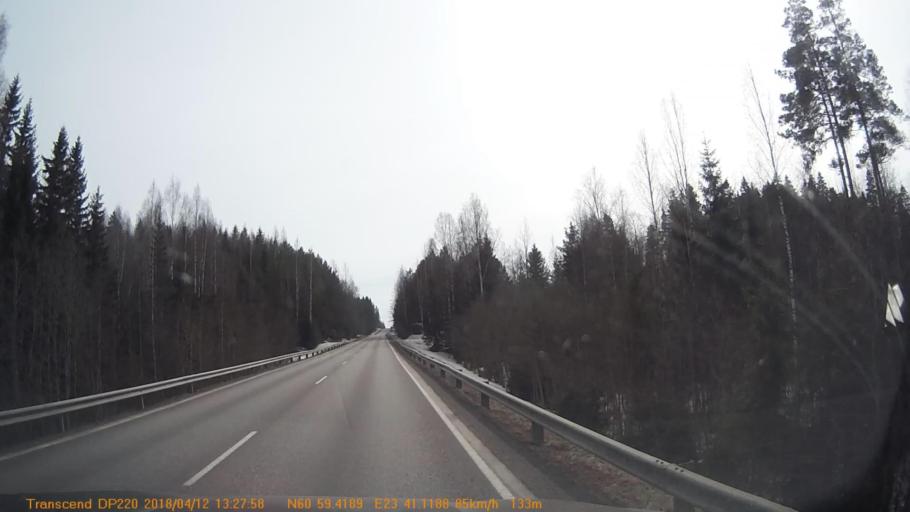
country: FI
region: Pirkanmaa
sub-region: Etelae-Pirkanmaa
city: Kylmaekoski
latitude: 60.9901
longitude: 23.6855
